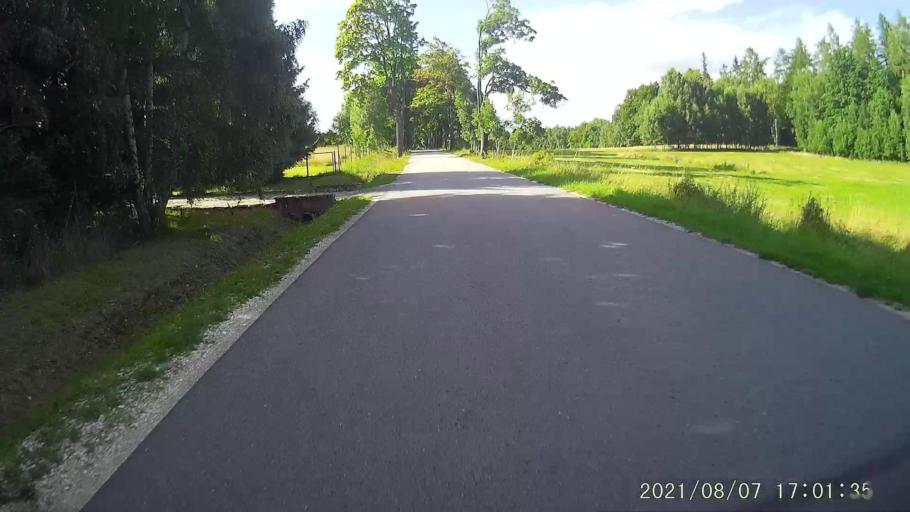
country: PL
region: Lower Silesian Voivodeship
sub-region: Powiat klodzki
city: Bystrzyca Klodzka
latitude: 50.2862
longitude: 16.5548
